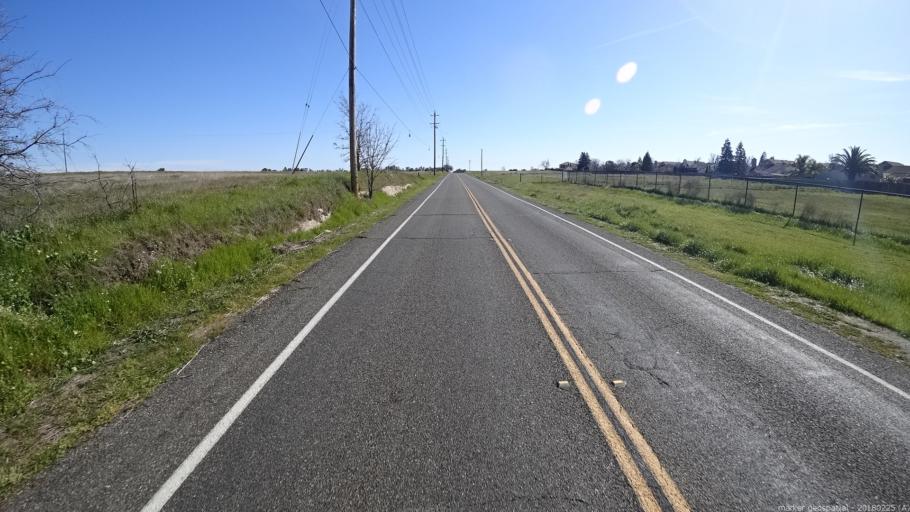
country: US
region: California
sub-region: Sacramento County
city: North Highlands
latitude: 38.7288
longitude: -121.3879
